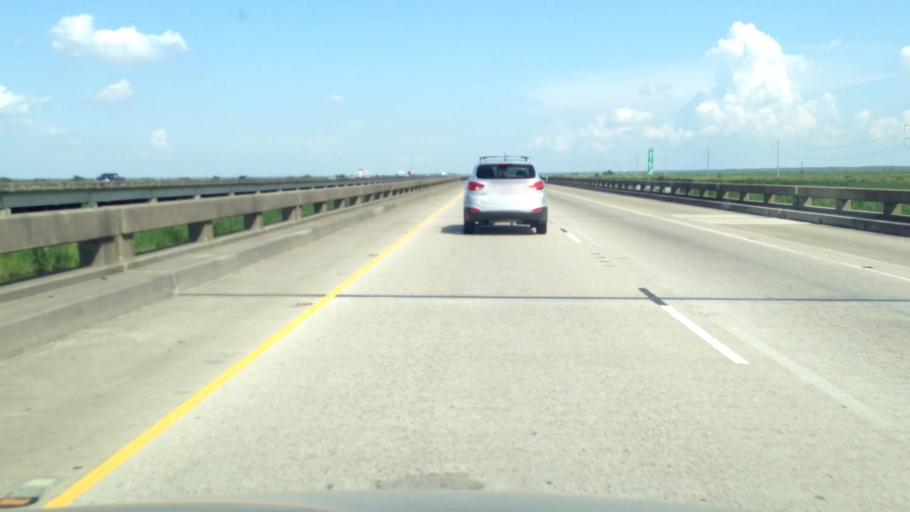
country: US
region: Louisiana
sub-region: Saint Charles Parish
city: Norco
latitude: 30.0482
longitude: -90.3616
